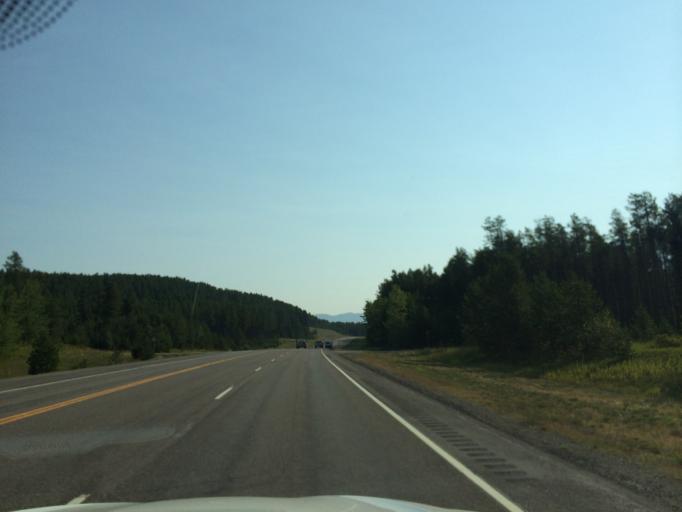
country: US
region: Montana
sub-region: Flathead County
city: Columbia Falls
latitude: 48.4464
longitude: -114.0341
